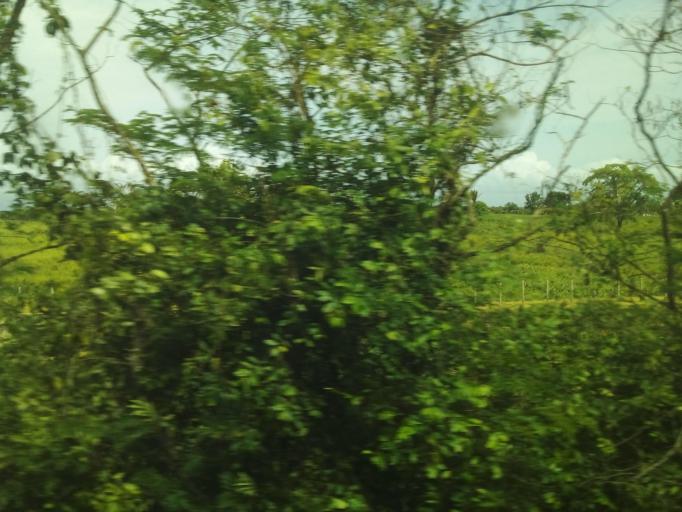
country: BR
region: Maranhao
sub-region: Anajatuba
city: Anajatuba
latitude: -3.4531
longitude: -44.5848
